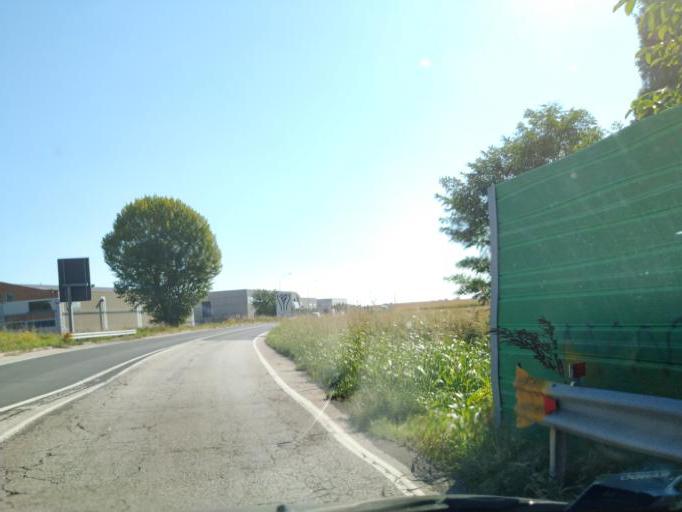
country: IT
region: Emilia-Romagna
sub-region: Provincia di Bologna
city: Decima
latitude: 44.6986
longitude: 11.2275
